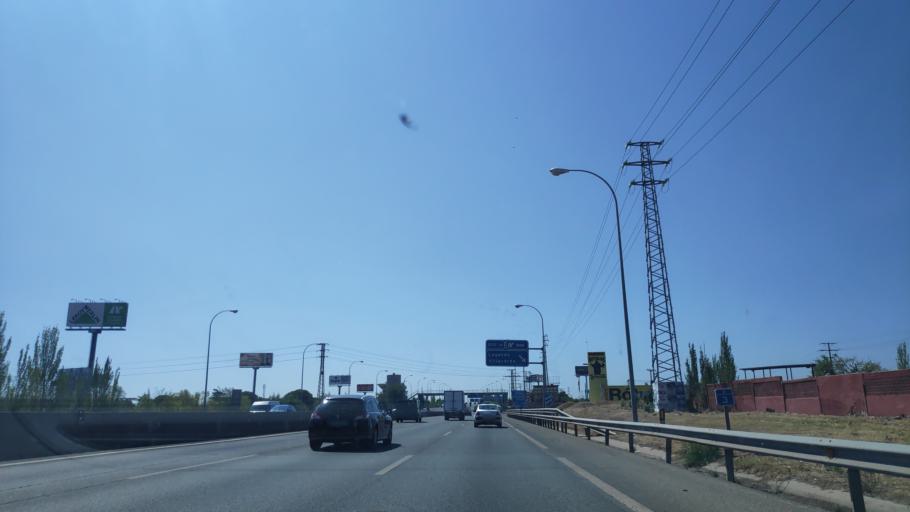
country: ES
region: Madrid
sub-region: Provincia de Madrid
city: Villaverde
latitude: 40.3470
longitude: -3.7233
